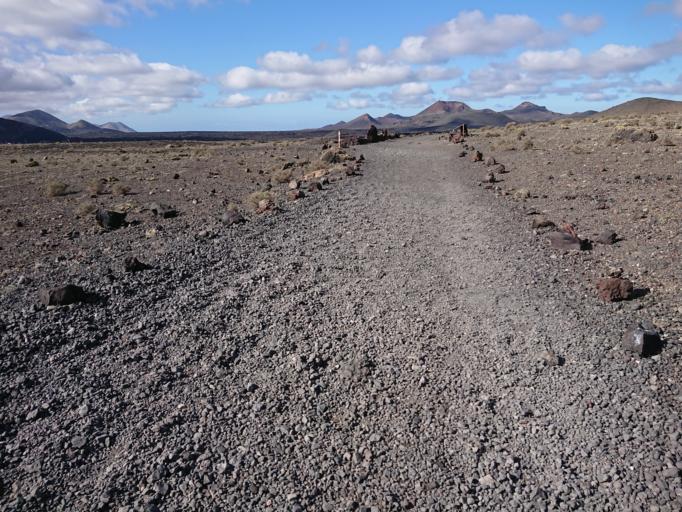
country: ES
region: Canary Islands
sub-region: Provincia de Las Palmas
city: Tias
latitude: 29.0028
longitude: -13.6798
